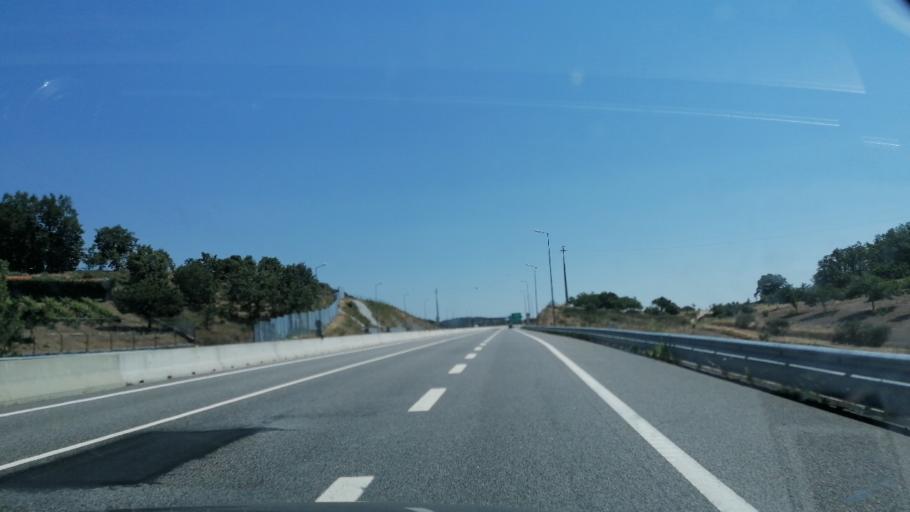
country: PT
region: Braganca
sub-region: Braganca Municipality
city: Braganca
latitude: 41.7605
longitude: -6.7988
